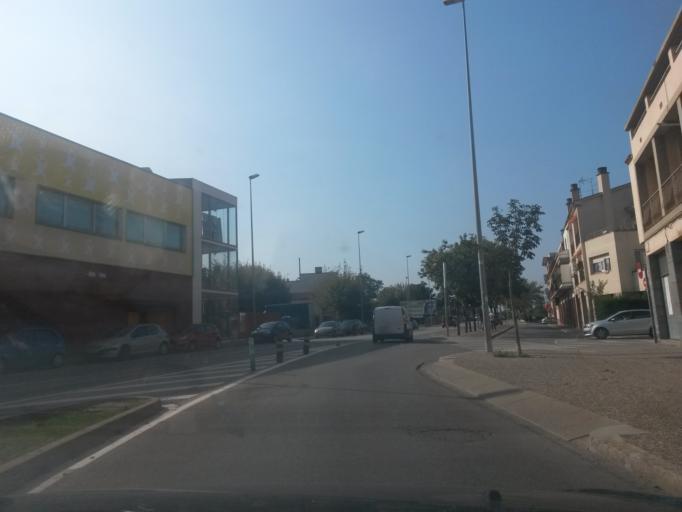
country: ES
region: Catalonia
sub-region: Provincia de Girona
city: Salt
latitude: 41.9678
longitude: 2.8106
